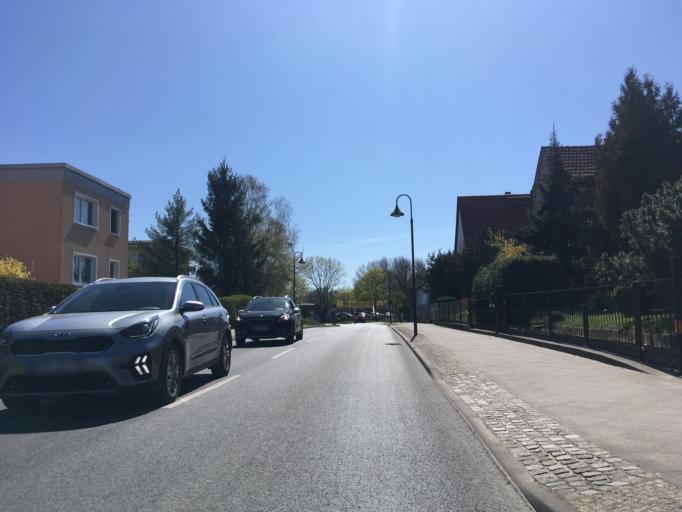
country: DE
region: Brandenburg
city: Bernau bei Berlin
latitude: 52.6688
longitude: 13.5581
